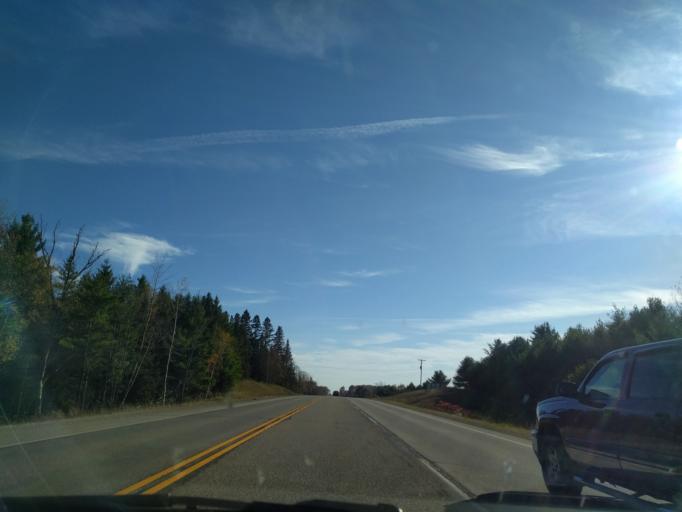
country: US
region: Wisconsin
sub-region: Marinette County
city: Niagara
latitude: 45.4860
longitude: -87.9867
